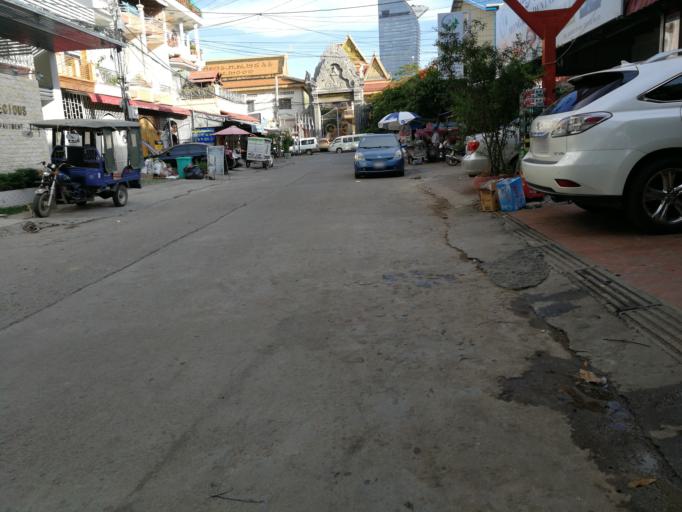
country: KH
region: Phnom Penh
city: Phnom Penh
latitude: 11.5805
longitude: 104.9186
